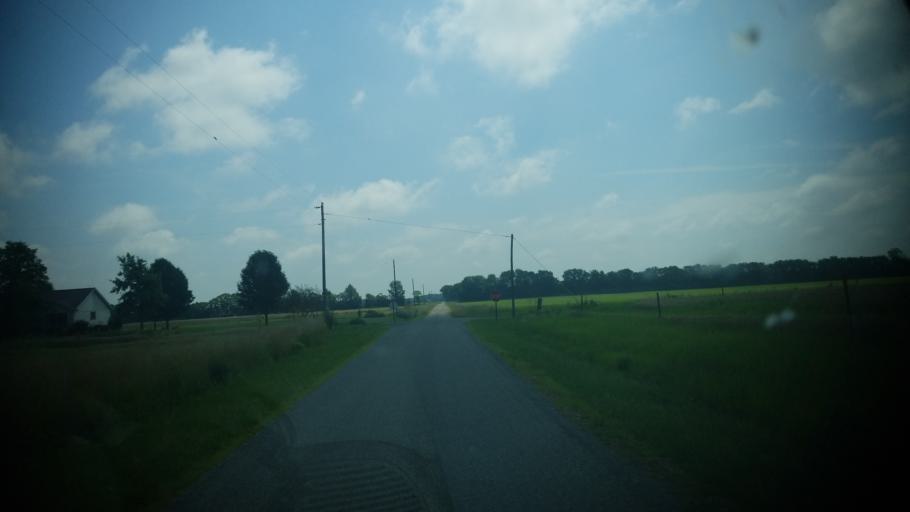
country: US
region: Illinois
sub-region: Wayne County
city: Fairfield
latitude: 38.5300
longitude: -88.3846
